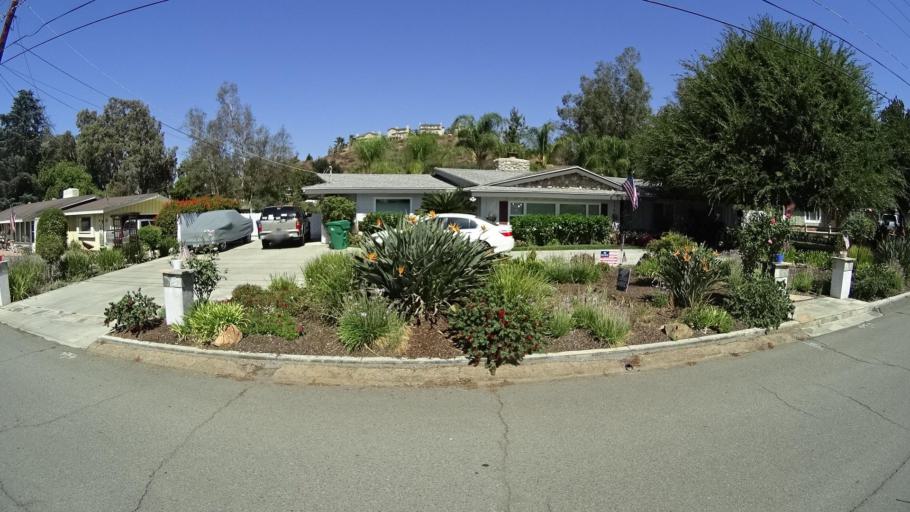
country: US
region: California
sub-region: San Diego County
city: Granite Hills
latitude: 32.8050
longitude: -116.9159
